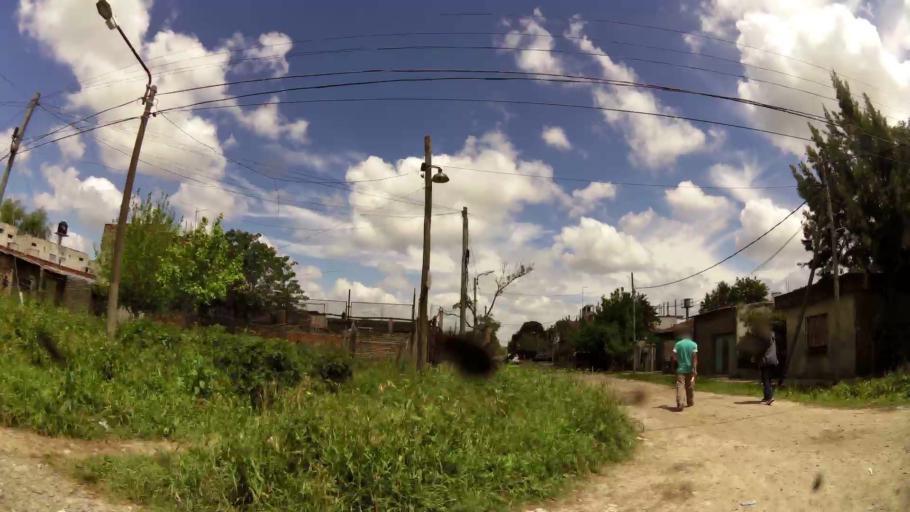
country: AR
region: Buenos Aires
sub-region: Partido de Quilmes
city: Quilmes
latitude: -34.8264
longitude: -58.2346
